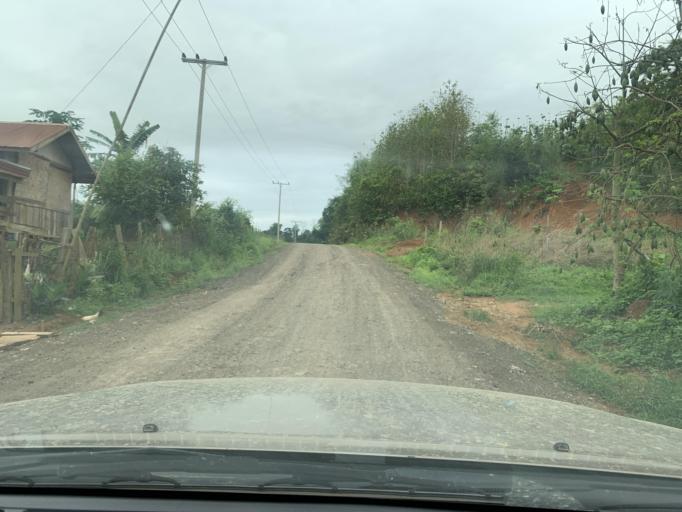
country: TH
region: Nan
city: Mae Charim
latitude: 18.4179
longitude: 101.4607
